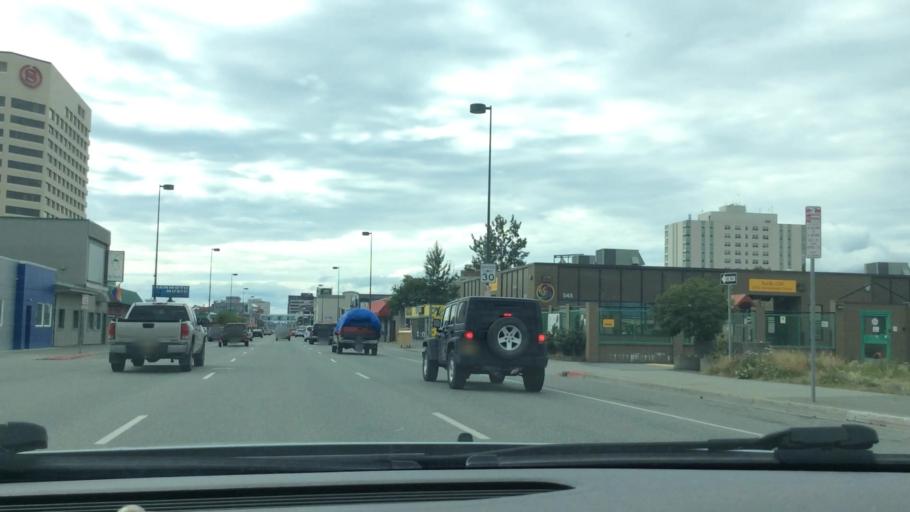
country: US
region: Alaska
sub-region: Anchorage Municipality
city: Anchorage
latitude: 61.2176
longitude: -149.8725
